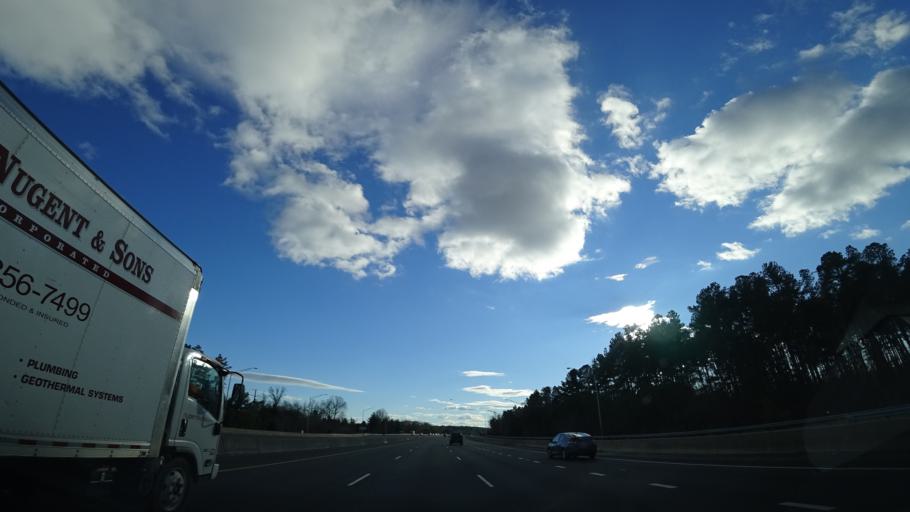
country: US
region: Virginia
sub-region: Fairfax County
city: Chantilly
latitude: 38.9130
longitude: -77.4307
